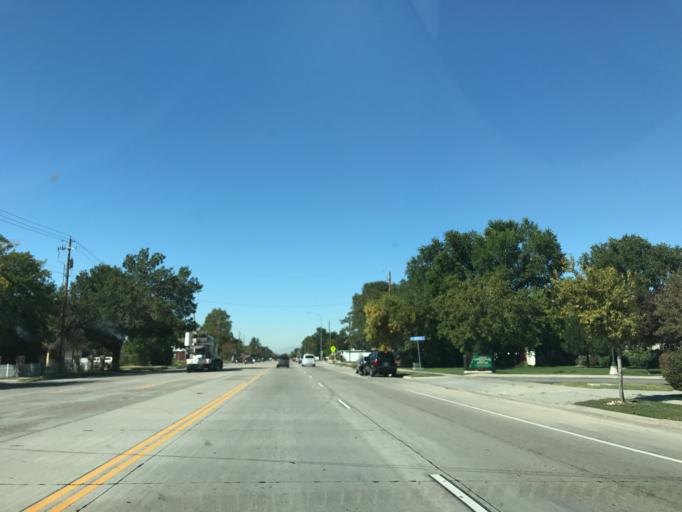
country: US
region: Utah
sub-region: Weber County
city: Ogden
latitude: 41.2442
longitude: -111.9540
